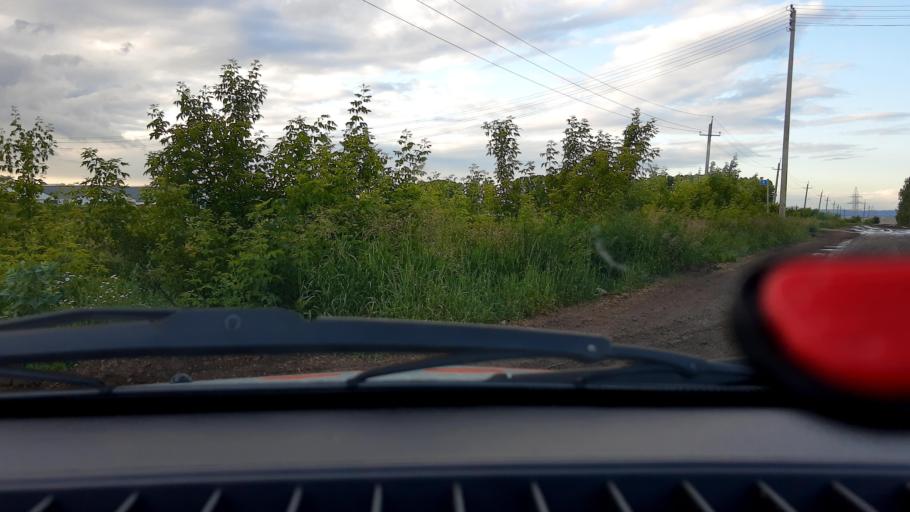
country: RU
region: Bashkortostan
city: Tolbazy
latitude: 54.1907
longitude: 55.8765
